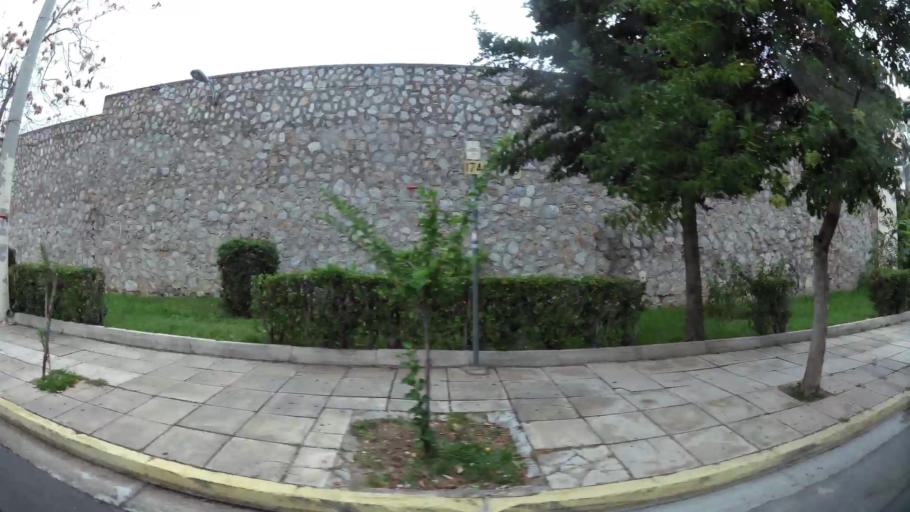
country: GR
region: Attica
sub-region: Nomos Piraios
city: Korydallos
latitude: 37.9835
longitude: 23.6482
